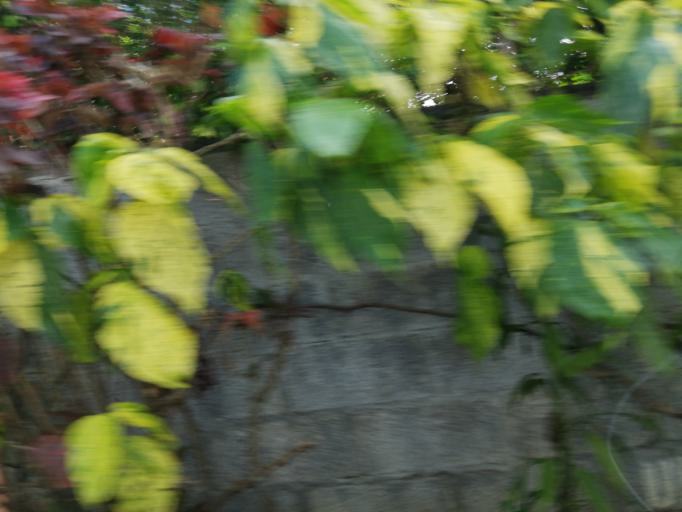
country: MU
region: Moka
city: Moka
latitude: -20.2251
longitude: 57.4736
